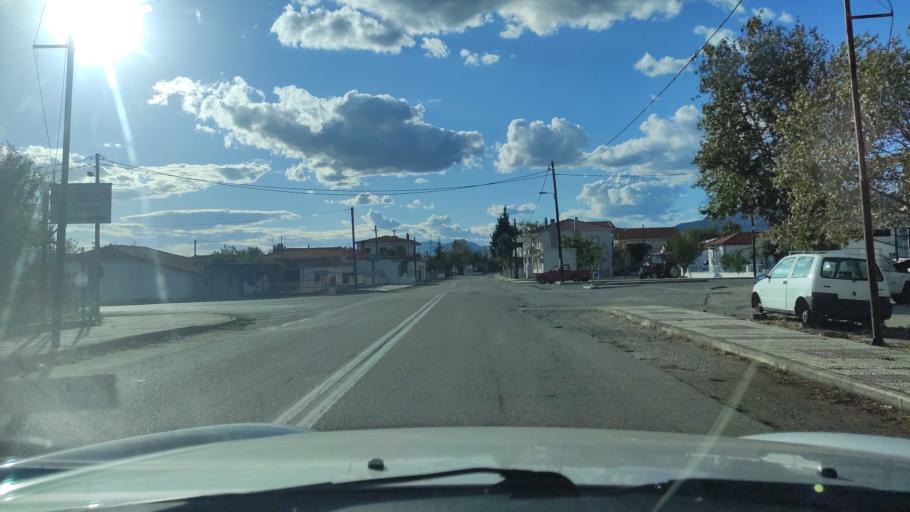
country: GR
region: East Macedonia and Thrace
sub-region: Nomos Xanthis
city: Selero
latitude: 41.1223
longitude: 25.0659
